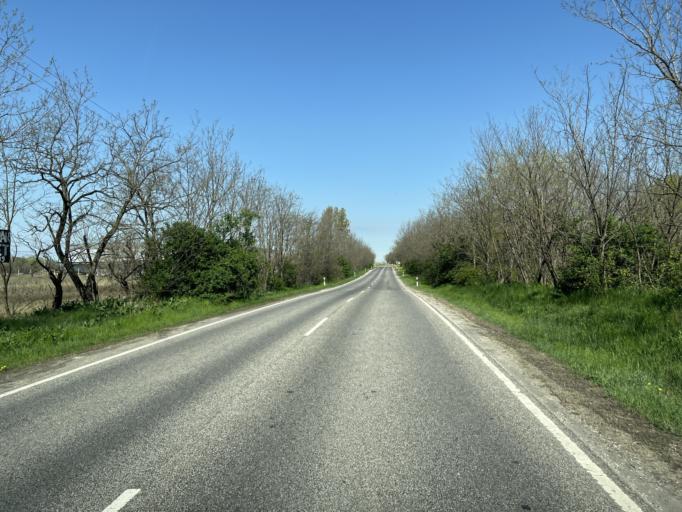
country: HU
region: Pest
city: Alsonemedi
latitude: 47.3385
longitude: 19.1765
